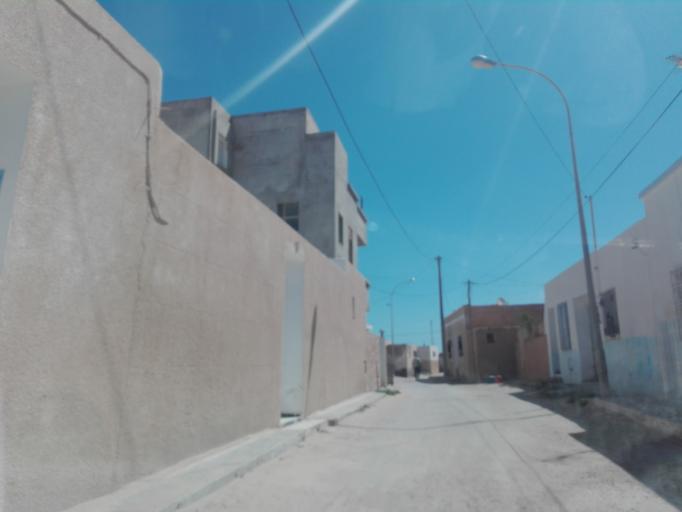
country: TN
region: Safaqis
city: Jabinyanah
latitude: 34.7456
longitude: 11.2945
